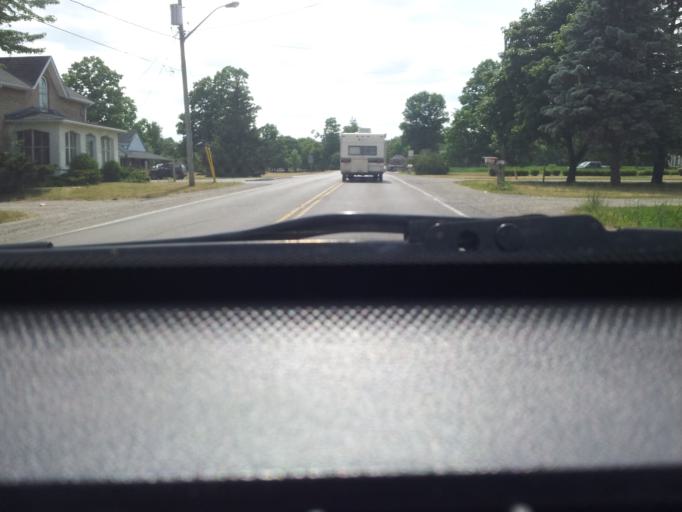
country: CA
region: Ontario
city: Brant
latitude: 43.1011
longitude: -80.4427
